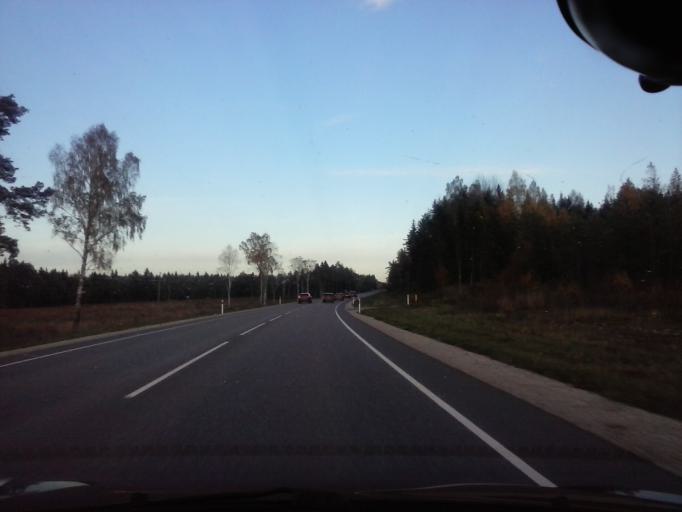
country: EE
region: Harju
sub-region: Nissi vald
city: Turba
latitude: 58.9787
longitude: 23.9594
